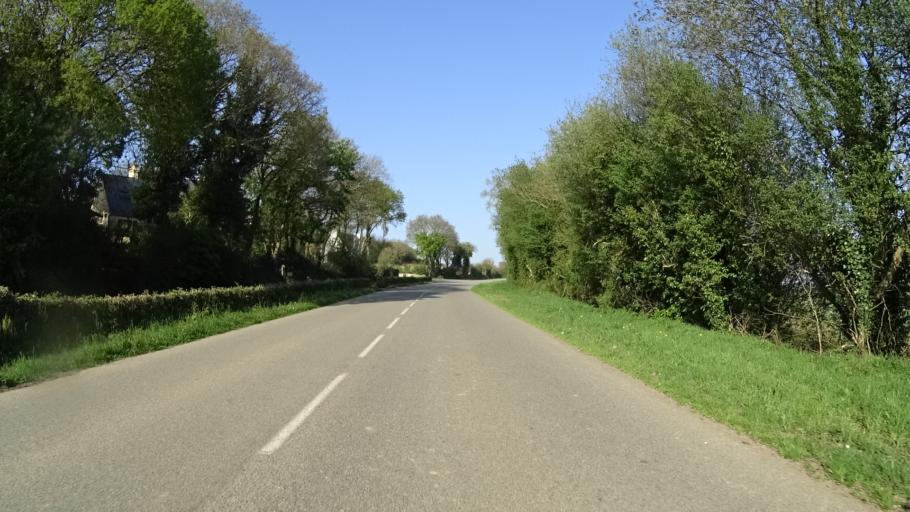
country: FR
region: Brittany
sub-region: Departement du Finistere
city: Daoulas
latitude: 48.3602
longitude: -4.2372
